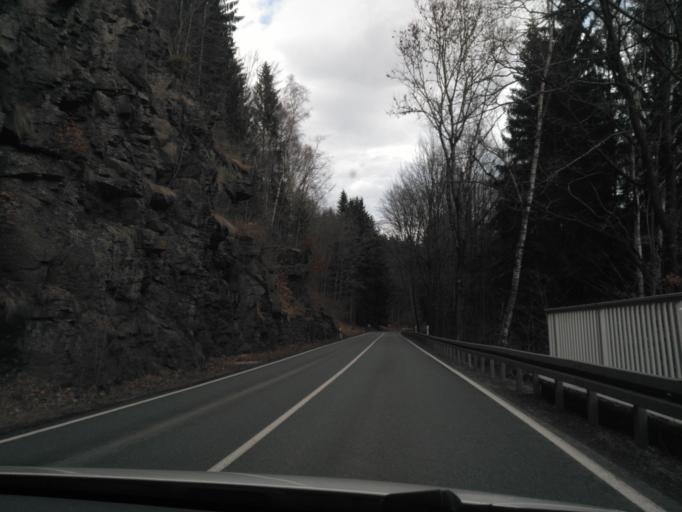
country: DE
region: Saxony
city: Wolkenstein
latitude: 50.6609
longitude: 13.0578
